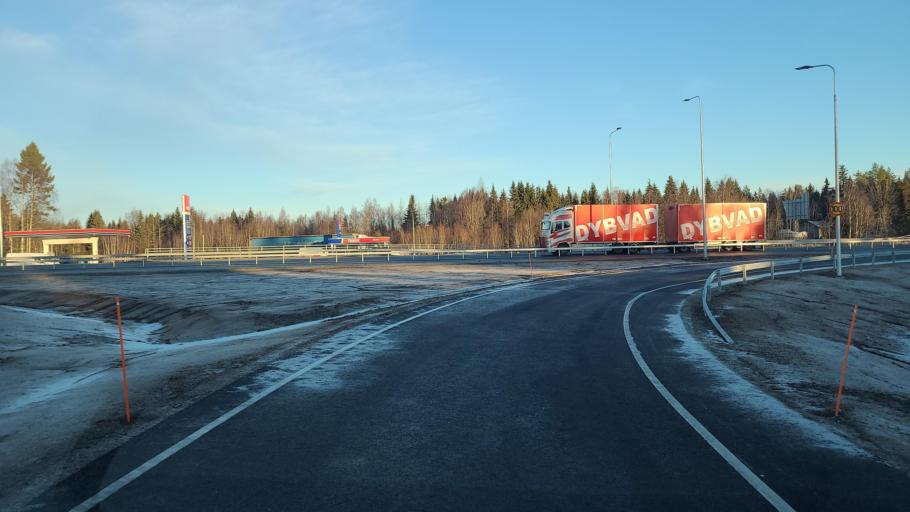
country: FI
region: Lapland
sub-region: Kemi-Tornio
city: Kemi
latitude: 65.6782
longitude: 24.7458
